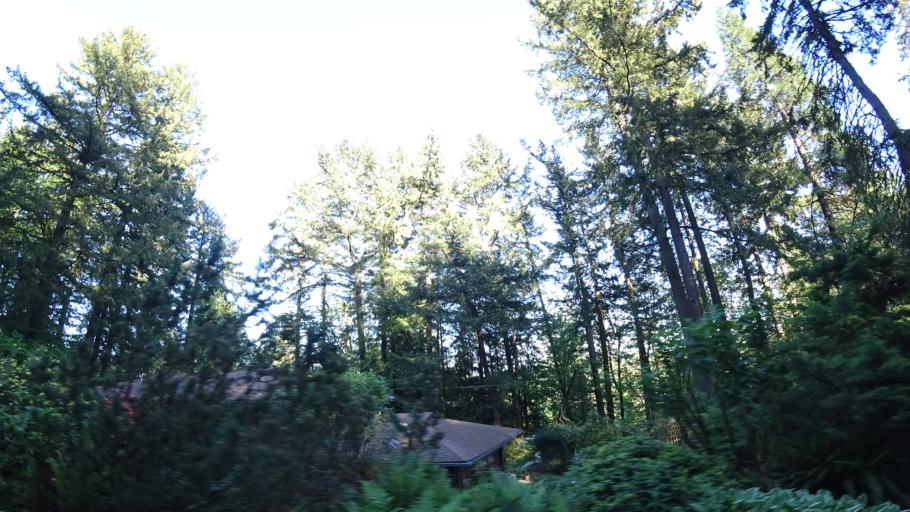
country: US
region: Oregon
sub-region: Washington County
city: West Slope
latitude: 45.4970
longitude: -122.7739
